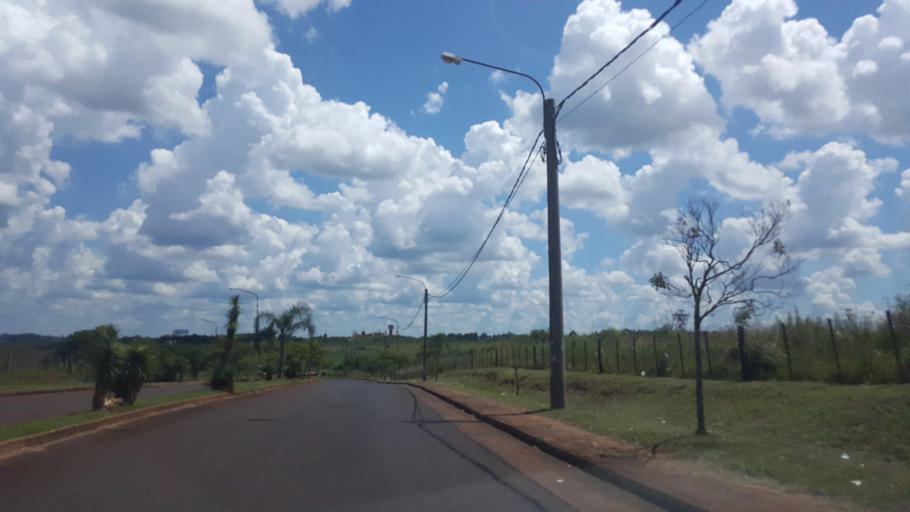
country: AR
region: Misiones
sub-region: Departamento de Capital
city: Posadas
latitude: -27.3810
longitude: -55.9628
